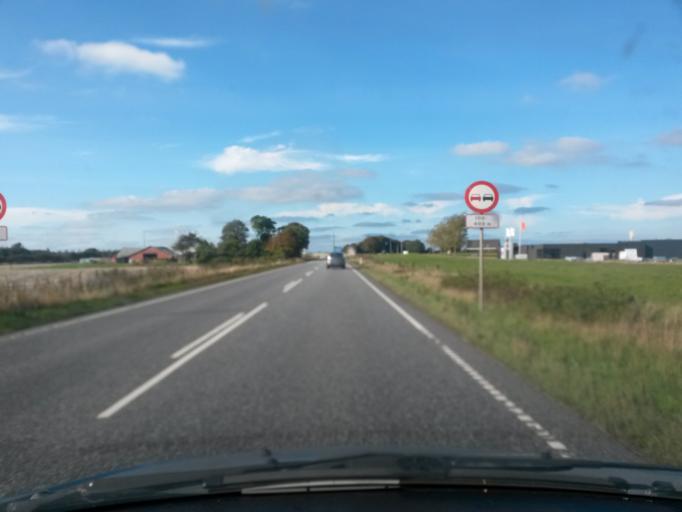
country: DK
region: Central Jutland
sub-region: Herning Kommune
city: Avlum
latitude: 56.2624
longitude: 8.7779
